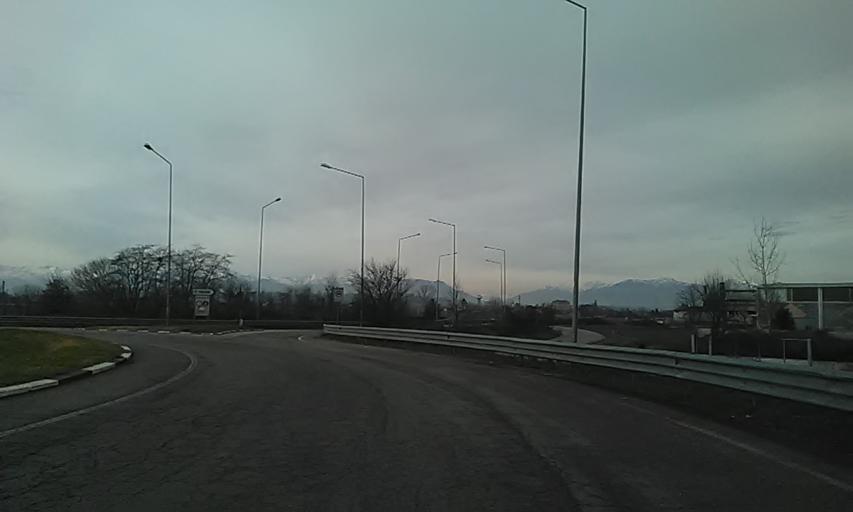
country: IT
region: Piedmont
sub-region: Provincia di Vercelli
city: Cigliano
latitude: 45.2977
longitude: 8.0228
